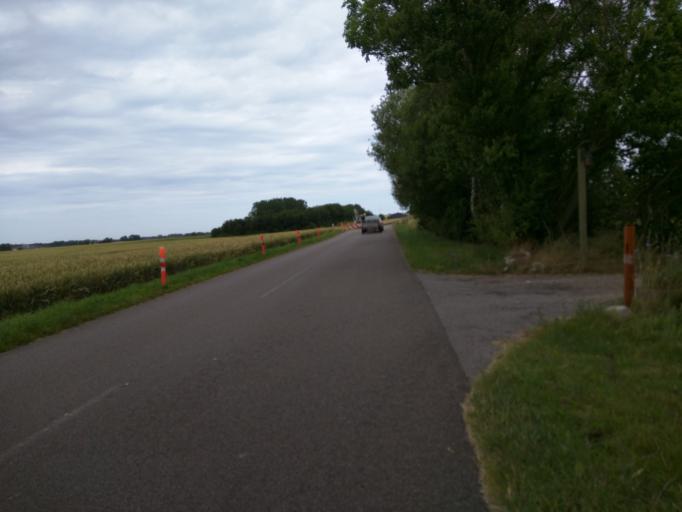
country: DK
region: Zealand
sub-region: Kalundborg Kommune
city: Svebolle
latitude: 55.6933
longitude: 11.3071
